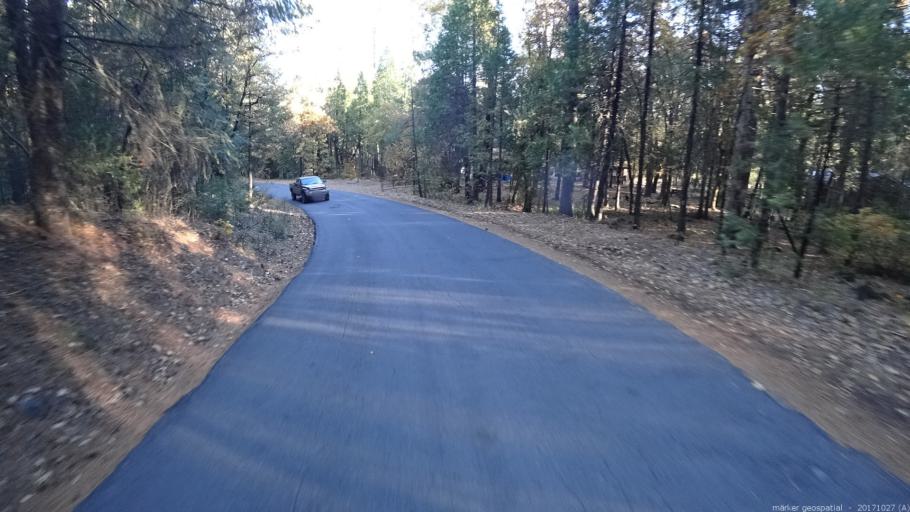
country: US
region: California
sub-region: Shasta County
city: Burney
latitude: 41.0102
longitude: -121.8967
